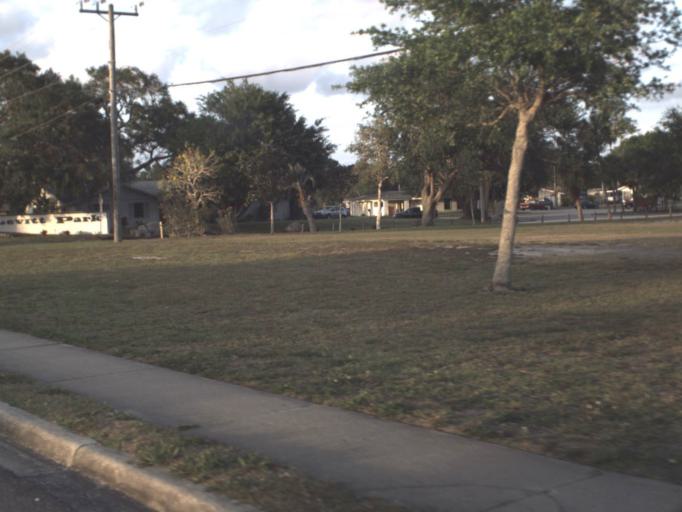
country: US
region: Florida
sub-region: Brevard County
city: Rockledge
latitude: 28.3156
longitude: -80.7427
